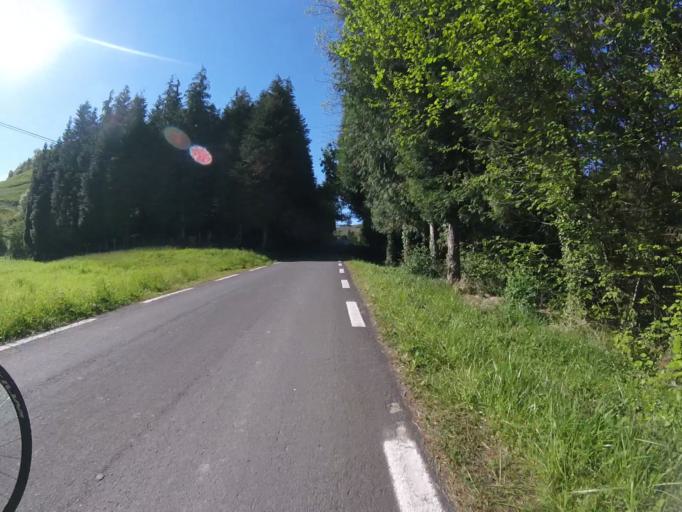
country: ES
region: Basque Country
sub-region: Provincia de Guipuzcoa
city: Aizarnazabal
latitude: 43.2267
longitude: -2.2141
